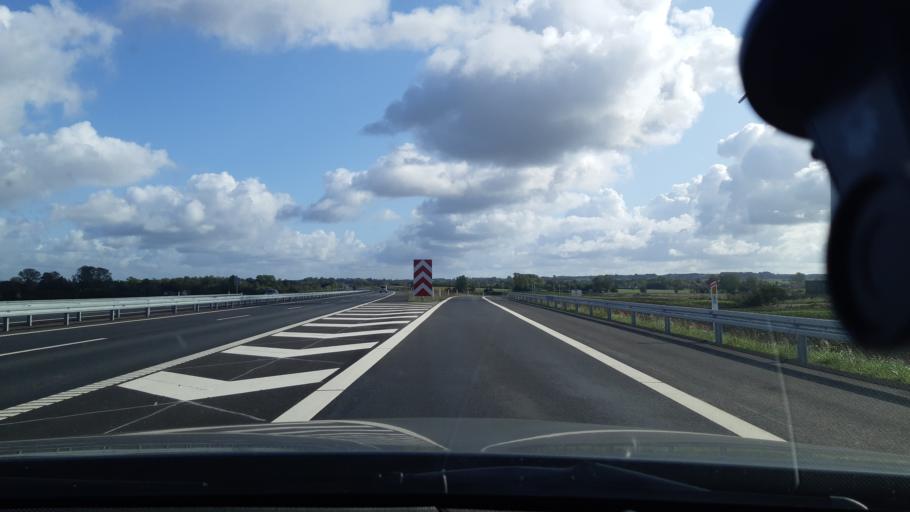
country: DK
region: Zealand
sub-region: Holbaek Kommune
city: Holbaek
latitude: 55.6586
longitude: 11.6245
